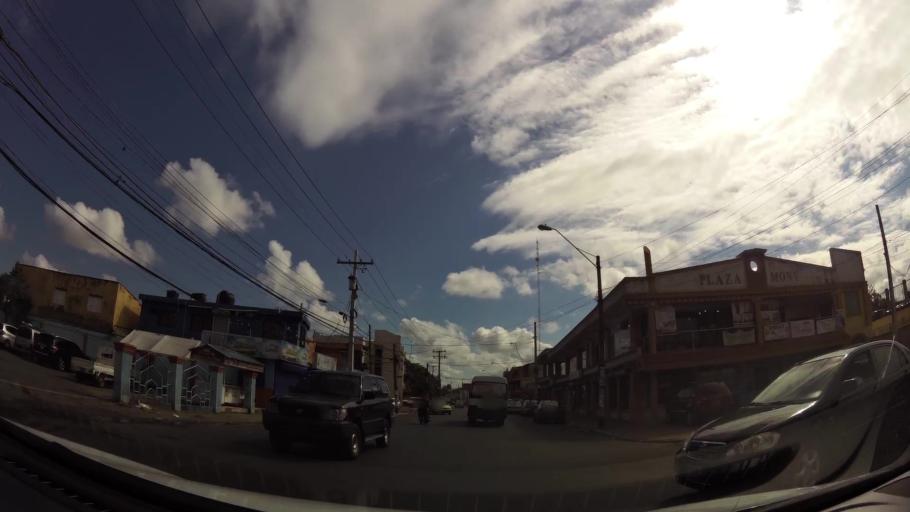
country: DO
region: Santo Domingo
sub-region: Santo Domingo
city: Santo Domingo Este
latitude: 18.4949
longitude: -69.8632
